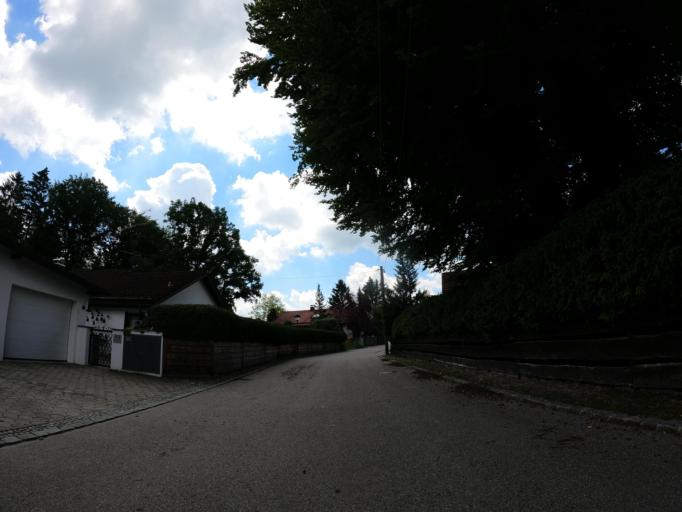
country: DE
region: Bavaria
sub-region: Upper Bavaria
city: Oberhaching
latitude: 47.9772
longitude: 11.5761
